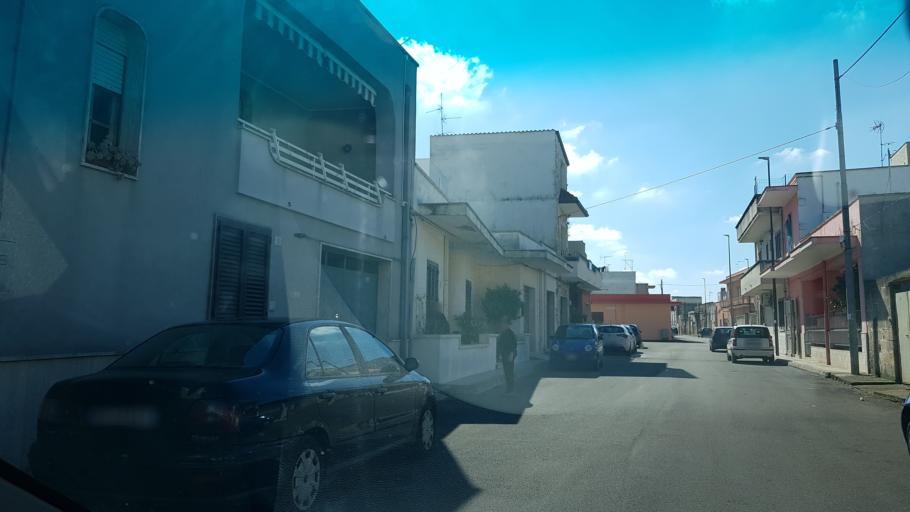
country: IT
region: Apulia
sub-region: Provincia di Lecce
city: Salice Salentino
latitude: 40.3865
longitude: 17.9668
